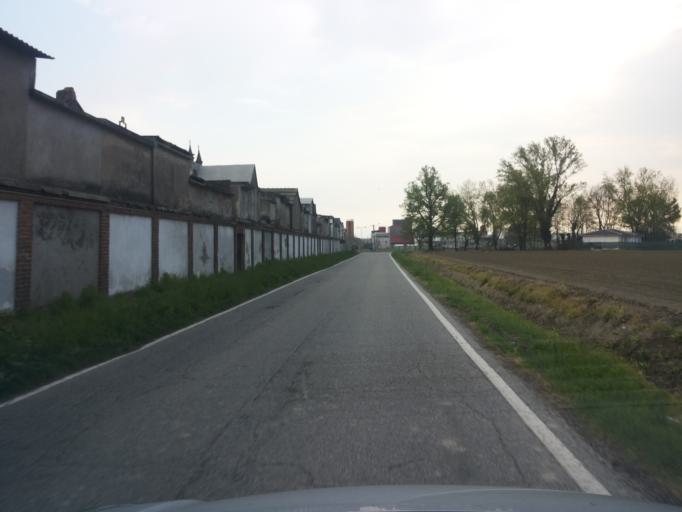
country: IT
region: Piedmont
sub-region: Provincia di Alessandria
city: Villanova Monferrato
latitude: 45.1849
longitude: 8.4870
